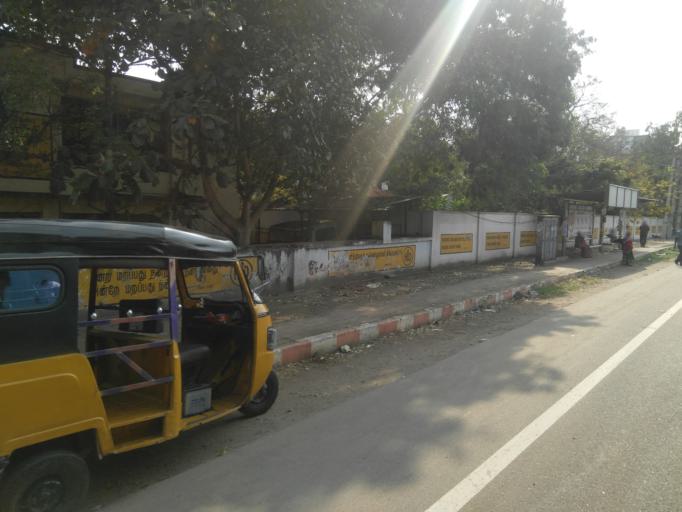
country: IN
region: Tamil Nadu
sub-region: Coimbatore
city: Coimbatore
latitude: 10.9957
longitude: 76.9770
